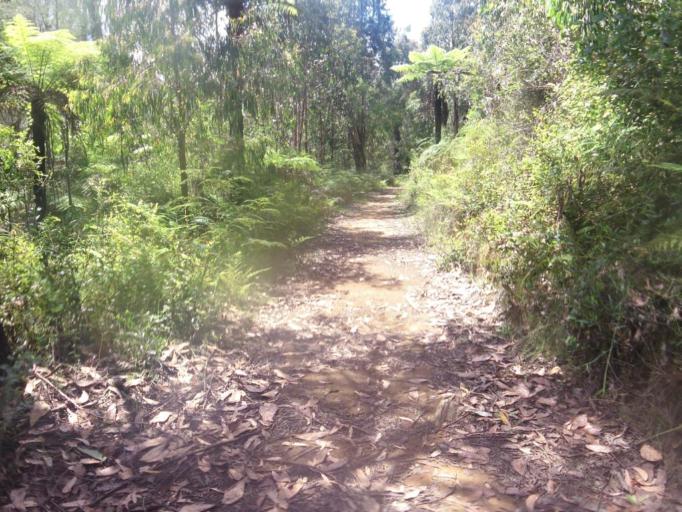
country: AU
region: Victoria
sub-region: Yarra Ranges
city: Millgrove
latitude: -37.5058
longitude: 145.7578
